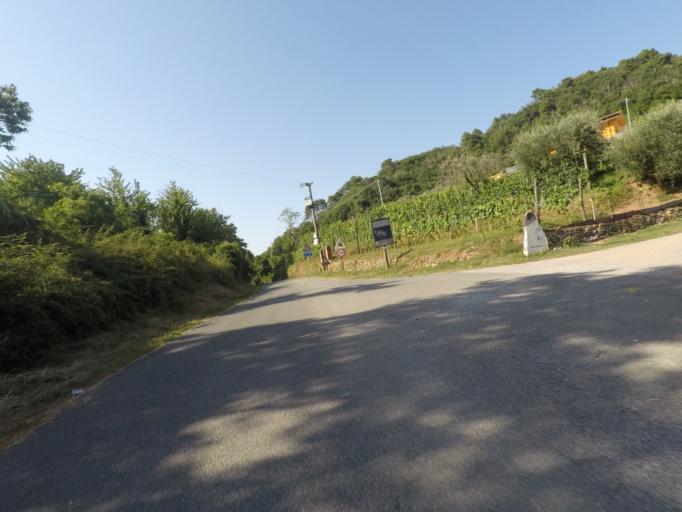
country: IT
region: Tuscany
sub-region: Provincia di Massa-Carrara
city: Carrara
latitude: 44.0851
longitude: 10.0637
